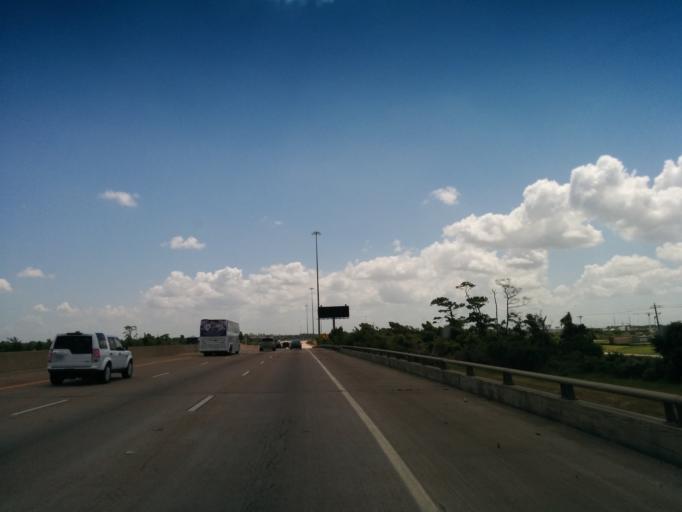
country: US
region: Texas
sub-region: Harris County
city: Highlands
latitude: 29.7921
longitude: -95.0800
